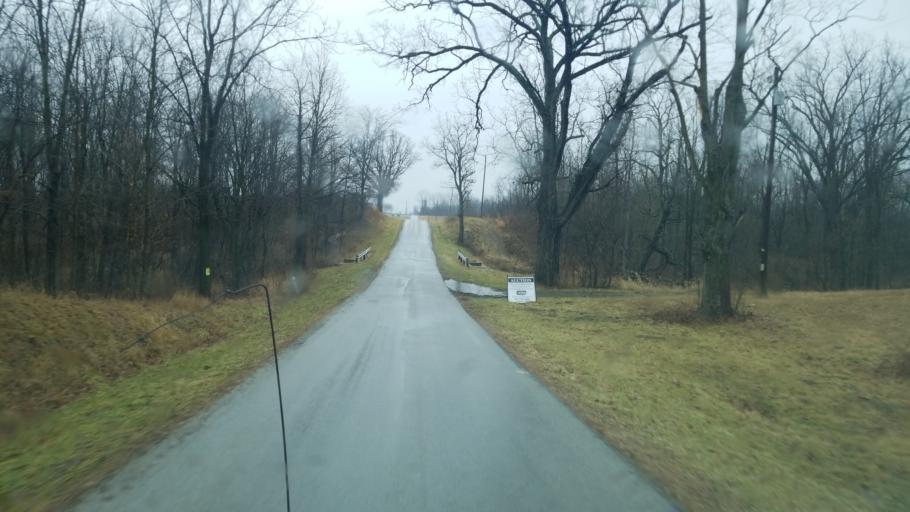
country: US
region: Ohio
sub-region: Wyandot County
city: Upper Sandusky
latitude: 40.7592
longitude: -83.3696
